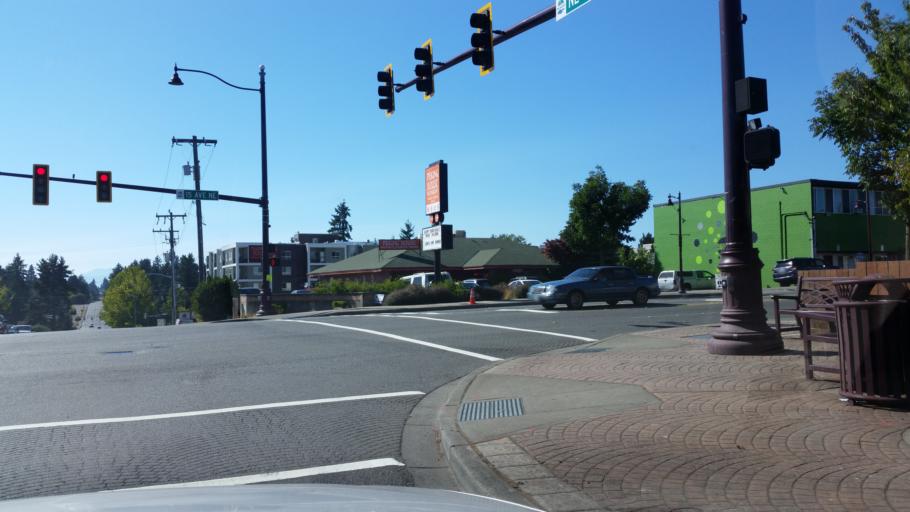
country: US
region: Washington
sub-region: King County
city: Shoreline
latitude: 47.7558
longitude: -122.3132
